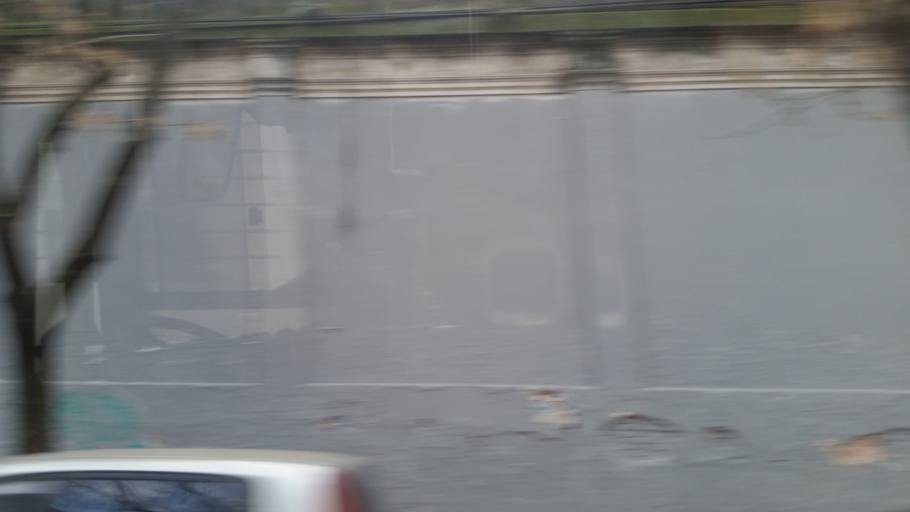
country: AR
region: Buenos Aires F.D.
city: Colegiales
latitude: -34.6073
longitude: -58.4242
